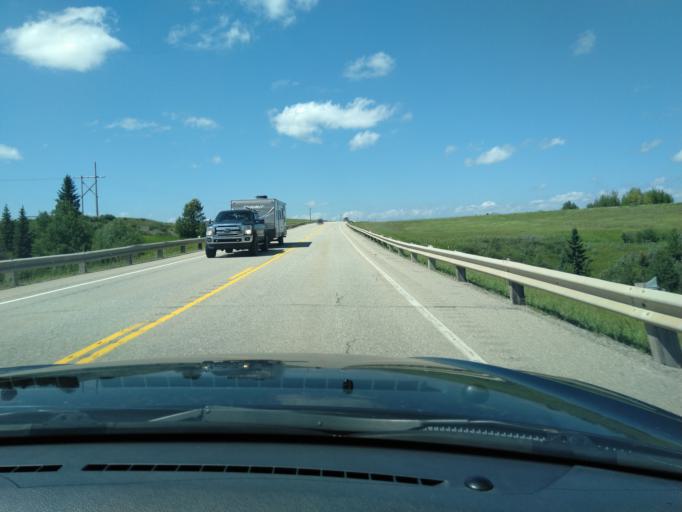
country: CA
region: Alberta
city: Cochrane
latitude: 51.2265
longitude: -114.5849
